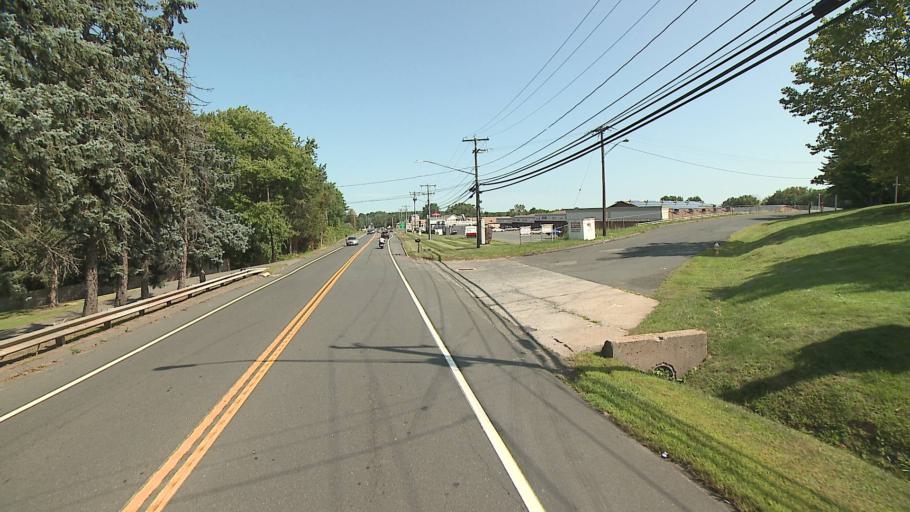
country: US
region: Connecticut
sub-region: Hartford County
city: Windsor Locks
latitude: 41.9280
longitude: -72.6060
